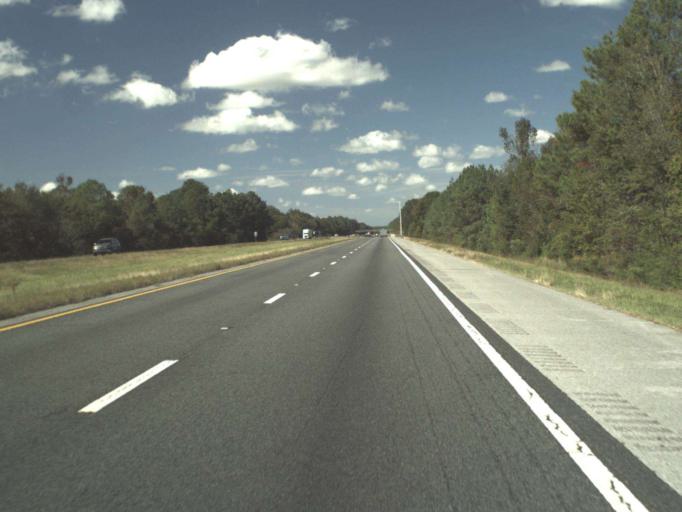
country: US
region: Florida
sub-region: Holmes County
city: Bonifay
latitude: 30.7552
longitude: -85.6131
